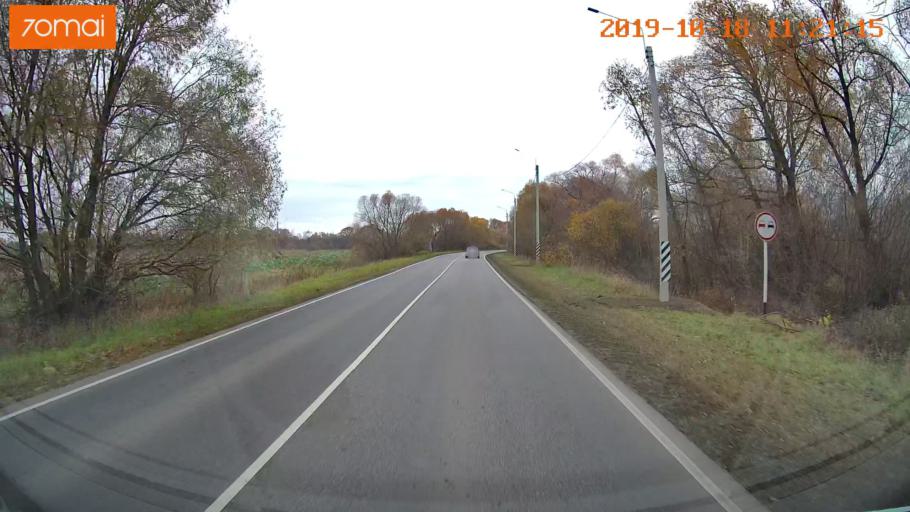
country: RU
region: Tula
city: Kimovsk
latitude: 54.0718
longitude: 38.5631
